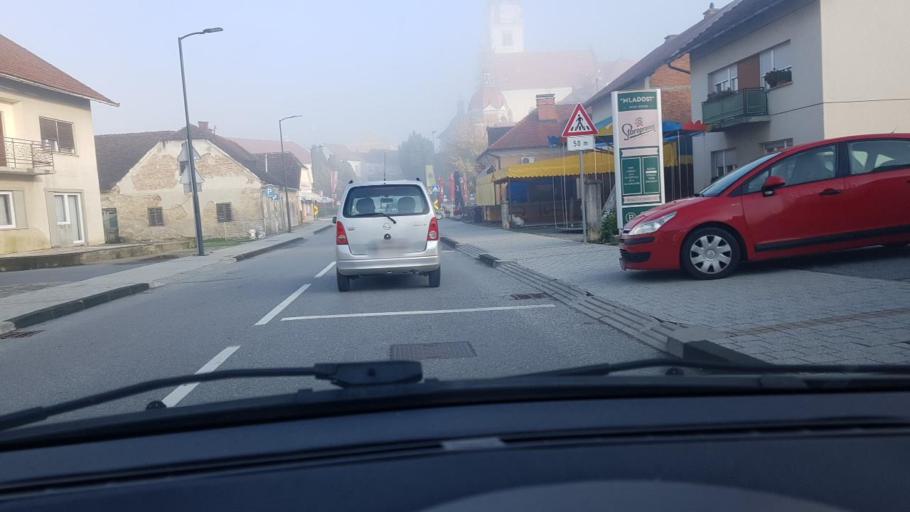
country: HR
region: Krapinsko-Zagorska
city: Marija Bistrica
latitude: 46.0030
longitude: 16.1192
